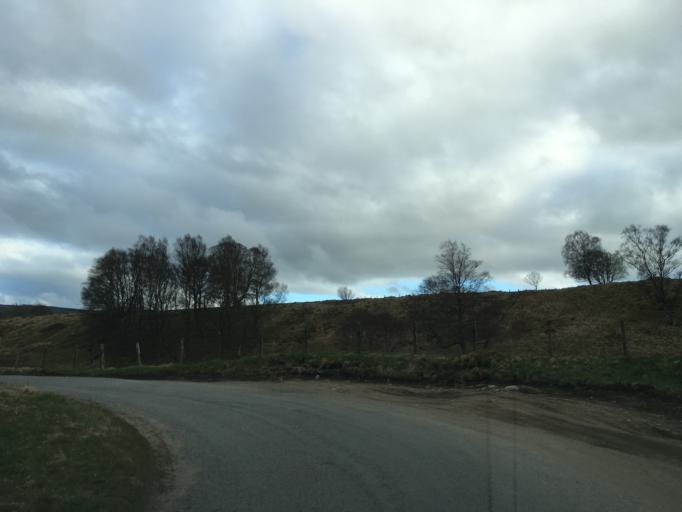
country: GB
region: Scotland
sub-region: Highland
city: Kingussie
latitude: 56.8042
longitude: -4.0875
